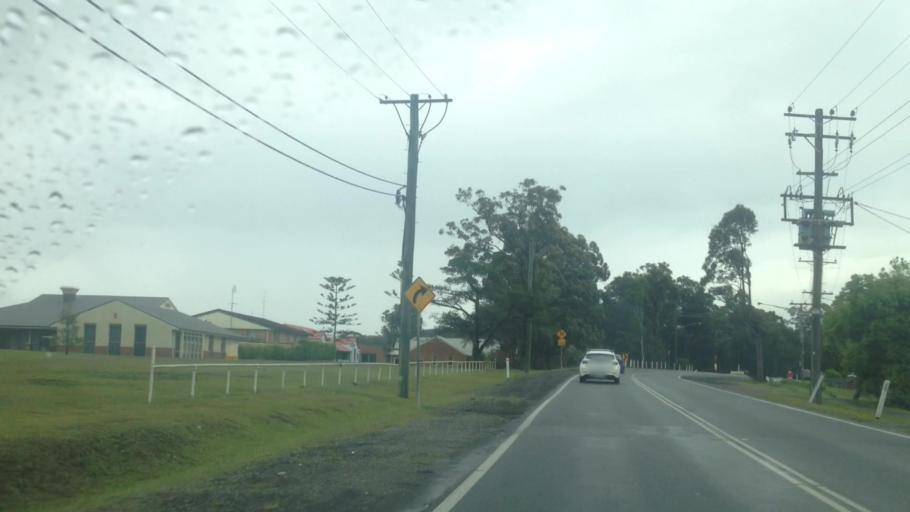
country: AU
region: New South Wales
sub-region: Wyong Shire
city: Charmhaven
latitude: -33.1695
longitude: 151.4765
